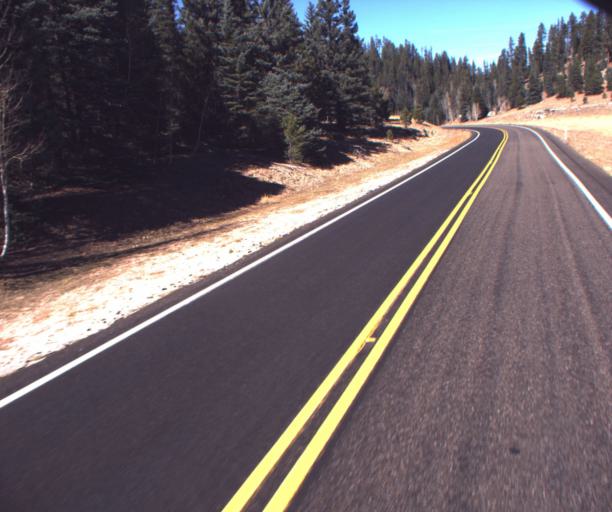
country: US
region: Arizona
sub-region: Coconino County
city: Grand Canyon
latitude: 36.5385
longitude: -112.1579
